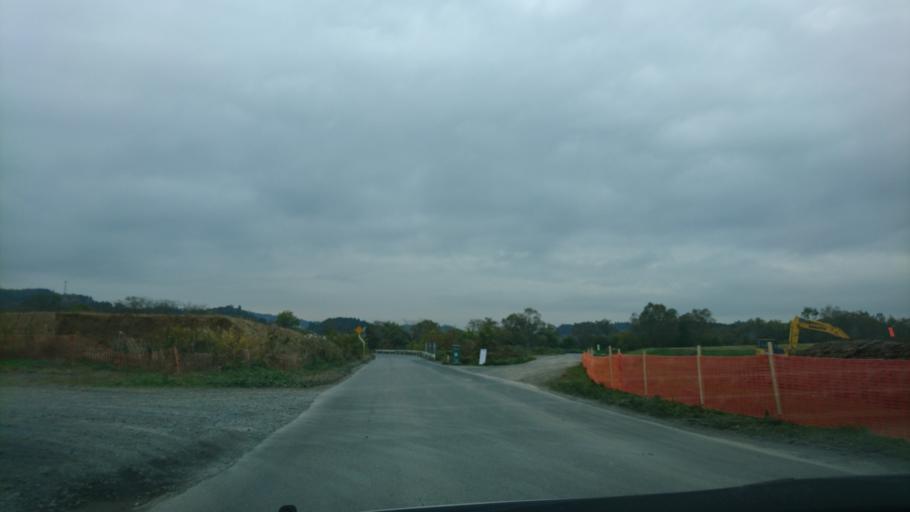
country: JP
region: Iwate
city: Ichinoseki
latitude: 38.9519
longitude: 141.1692
